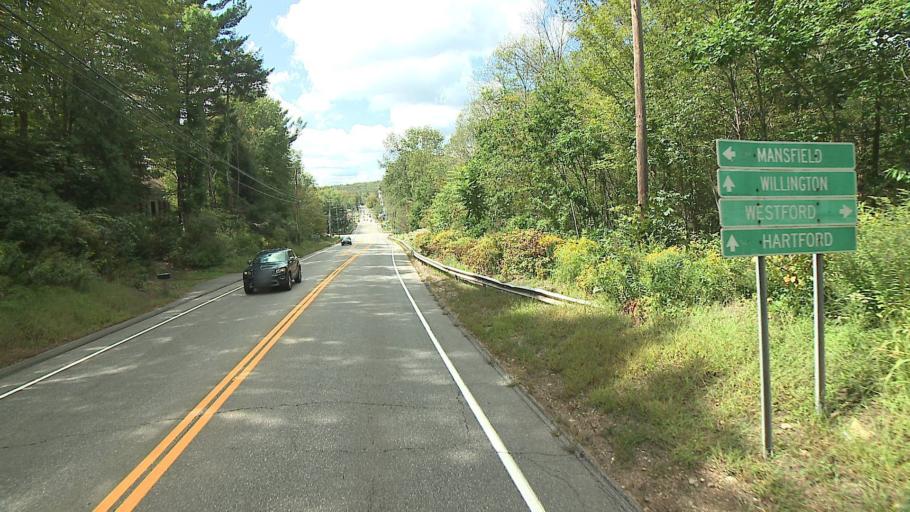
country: US
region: Connecticut
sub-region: Tolland County
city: Storrs
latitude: 41.8648
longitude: -72.1584
